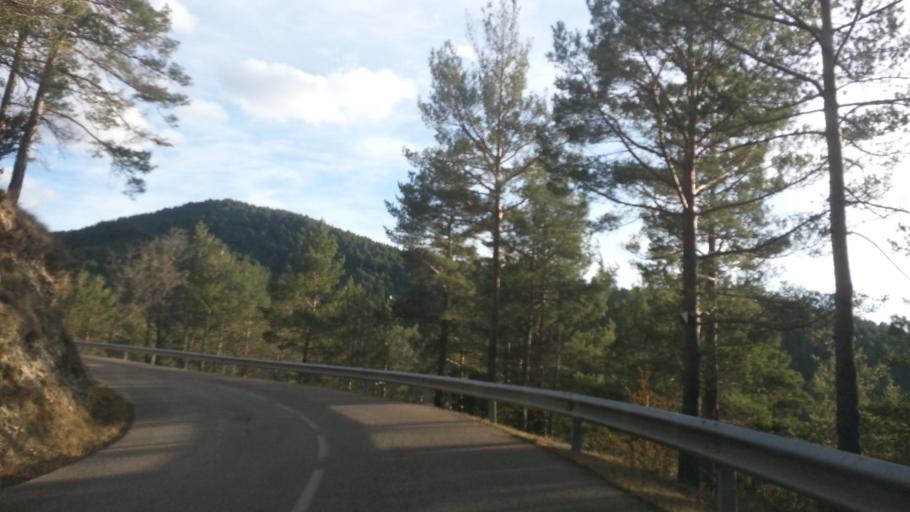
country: ES
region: Catalonia
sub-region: Provincia de Girona
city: Toses
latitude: 42.2483
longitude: 2.0376
